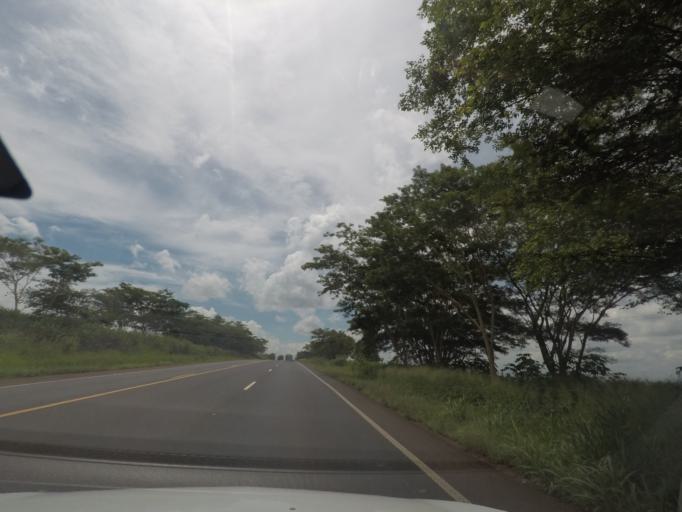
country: BR
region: Sao Paulo
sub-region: Barretos
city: Barretos
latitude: -20.3971
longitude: -48.6377
